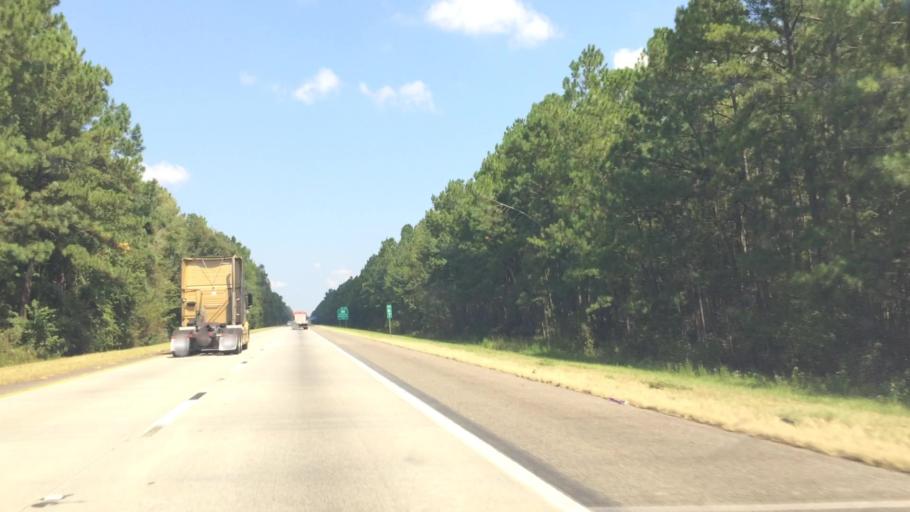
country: US
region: South Carolina
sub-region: Dorchester County
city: Saint George
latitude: 33.0652
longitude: -80.6611
